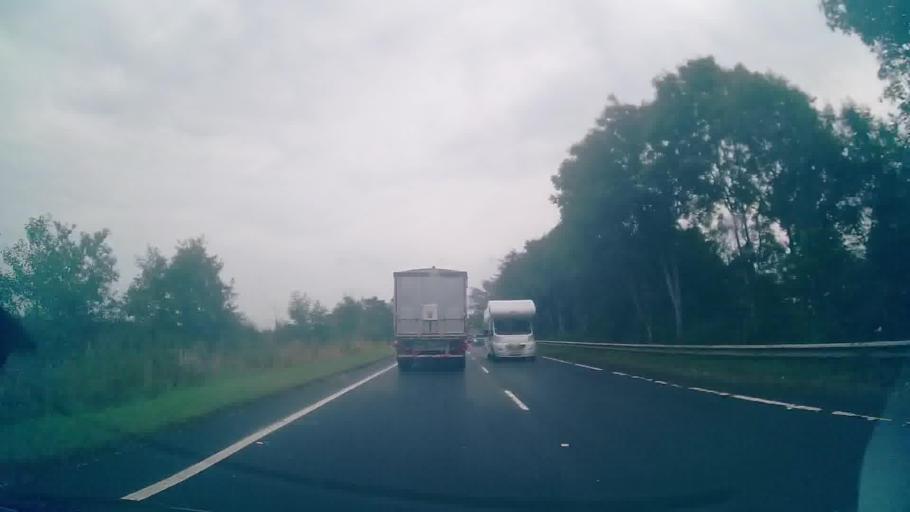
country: GB
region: Scotland
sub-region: Dumfries and Galloway
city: Gretna
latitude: 54.9936
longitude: -3.1041
